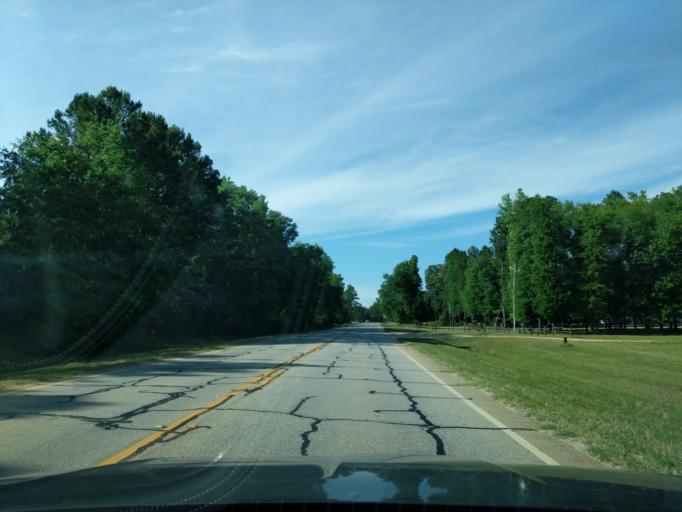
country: US
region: Georgia
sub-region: Jefferson County
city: Wrens
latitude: 33.2479
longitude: -82.3873
